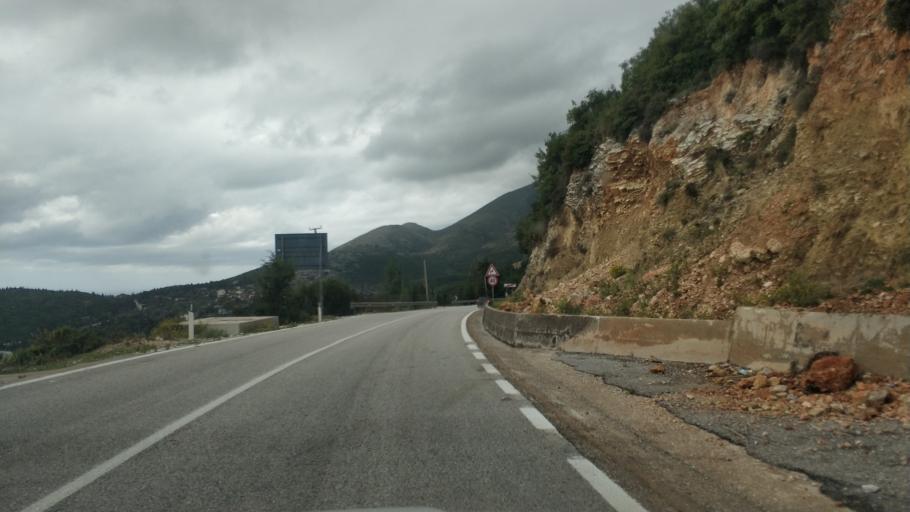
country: AL
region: Vlore
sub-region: Rrethi i Vlores
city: Himare
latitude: 40.1409
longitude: 19.6883
